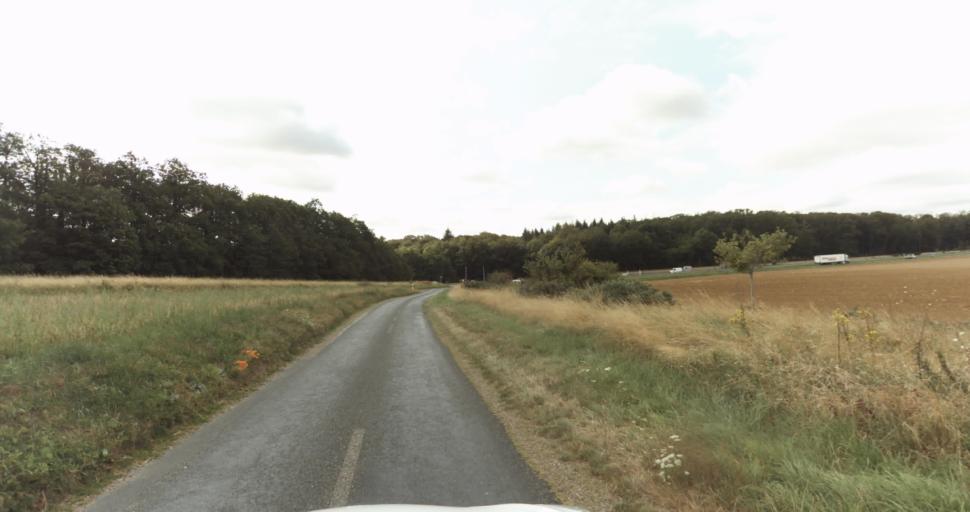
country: FR
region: Haute-Normandie
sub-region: Departement de l'Eure
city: Tillieres-sur-Avre
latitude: 48.7761
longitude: 1.1055
